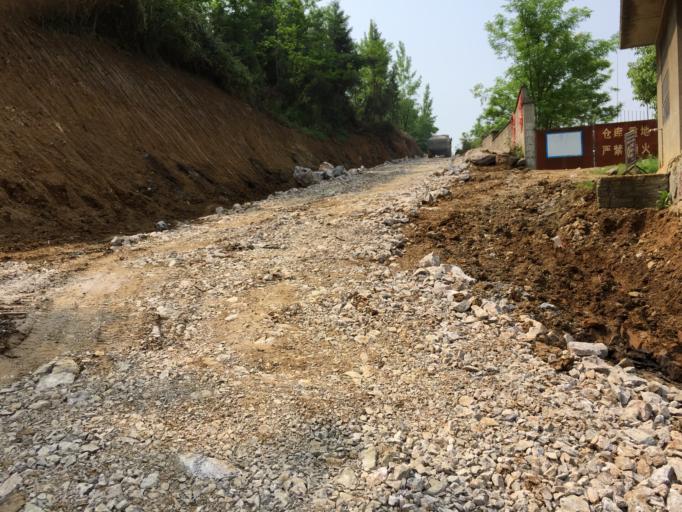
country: CN
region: Guizhou Sheng
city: Zhongba
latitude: 27.9614
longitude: 108.2215
